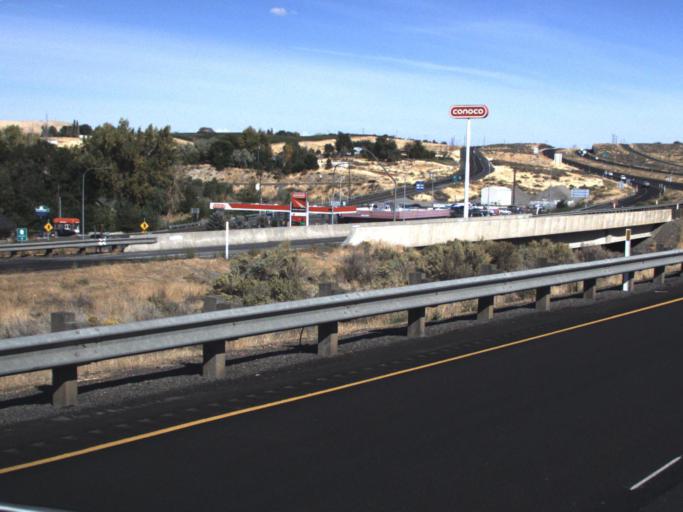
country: US
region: Washington
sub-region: Benton County
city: Benton City
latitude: 46.2510
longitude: -119.4765
